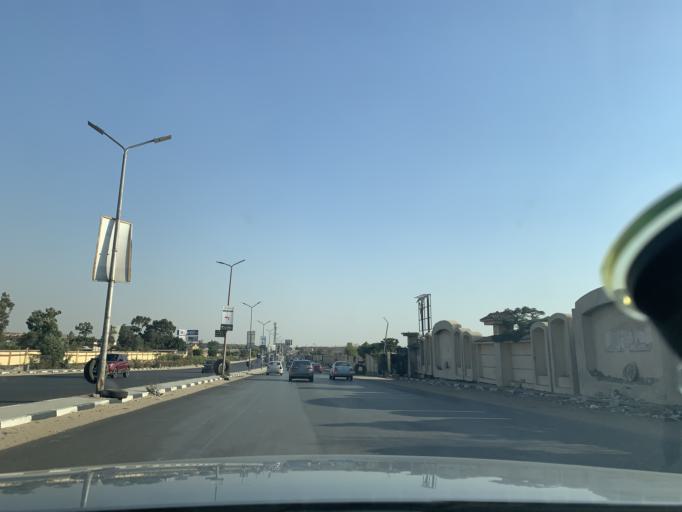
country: EG
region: Muhafazat al Qahirah
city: Cairo
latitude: 30.0303
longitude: 31.3543
